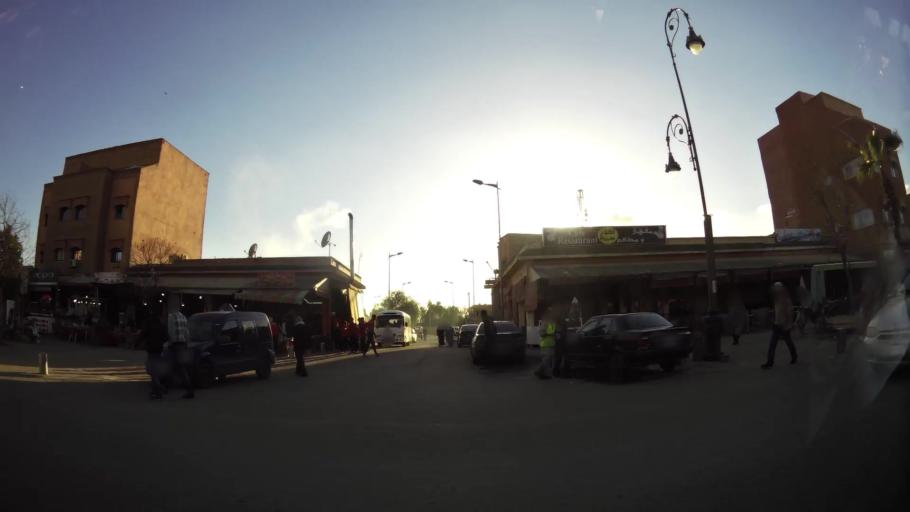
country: MA
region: Marrakech-Tensift-Al Haouz
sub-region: Kelaa-Des-Sraghna
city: Sidi Abdallah
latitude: 32.2379
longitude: -7.9591
